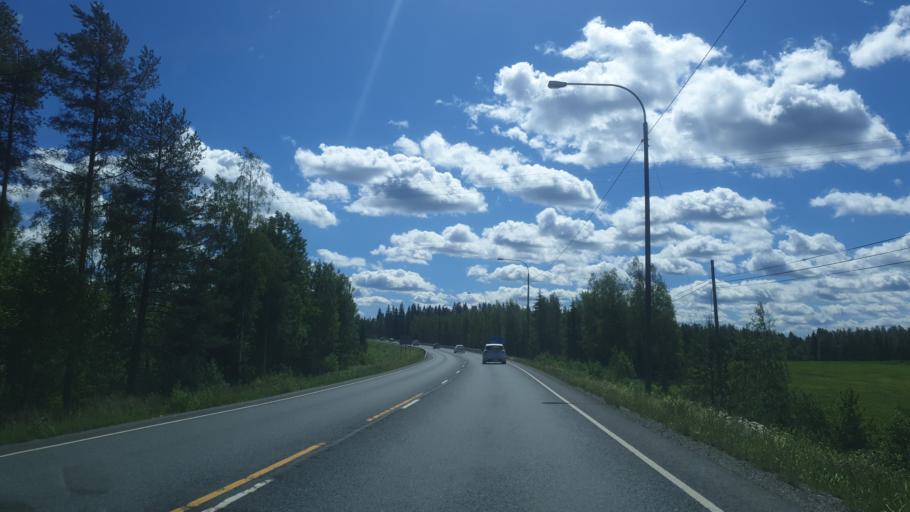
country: FI
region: Northern Savo
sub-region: Varkaus
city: Leppaevirta
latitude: 62.5469
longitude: 27.6237
